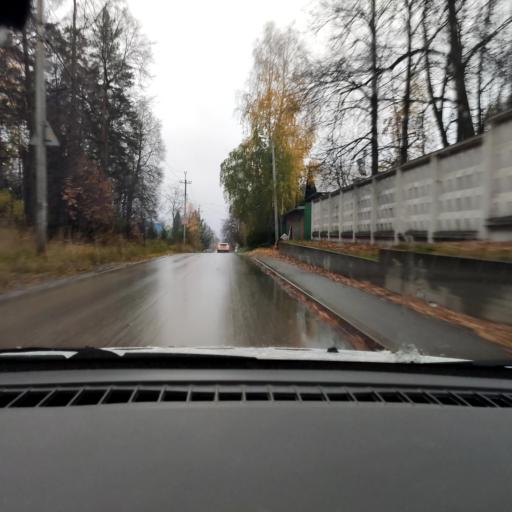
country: RU
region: Perm
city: Kondratovo
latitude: 58.0520
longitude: 56.1217
